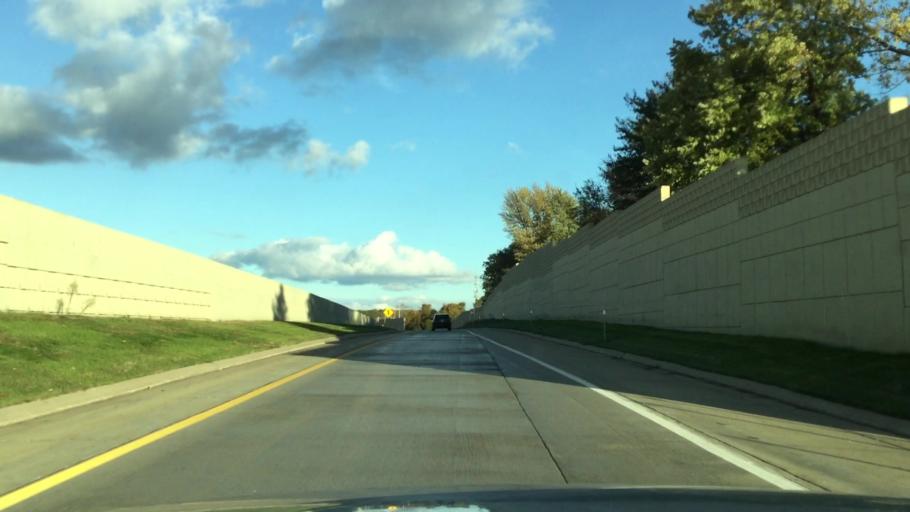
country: US
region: Michigan
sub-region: Kalamazoo County
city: Portage
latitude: 42.2364
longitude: -85.5874
